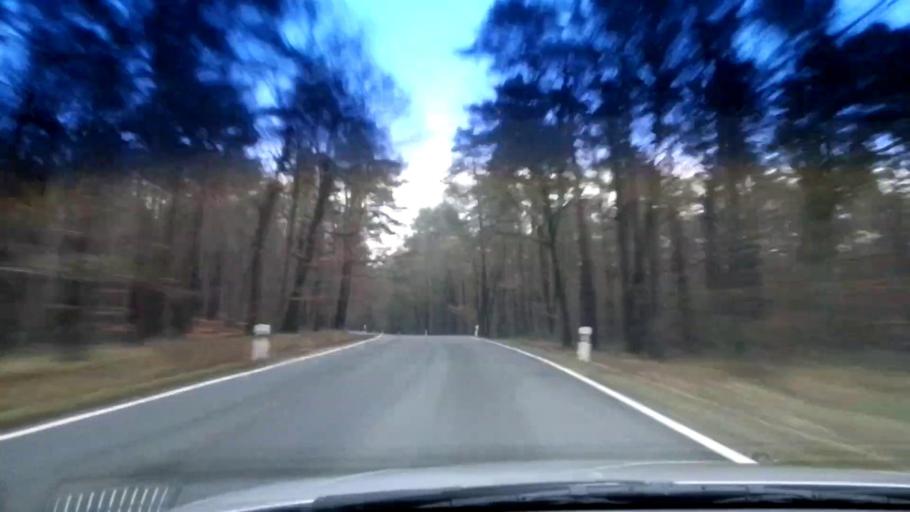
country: DE
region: Bavaria
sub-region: Upper Franconia
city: Pommersfelden
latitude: 49.7943
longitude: 10.7863
